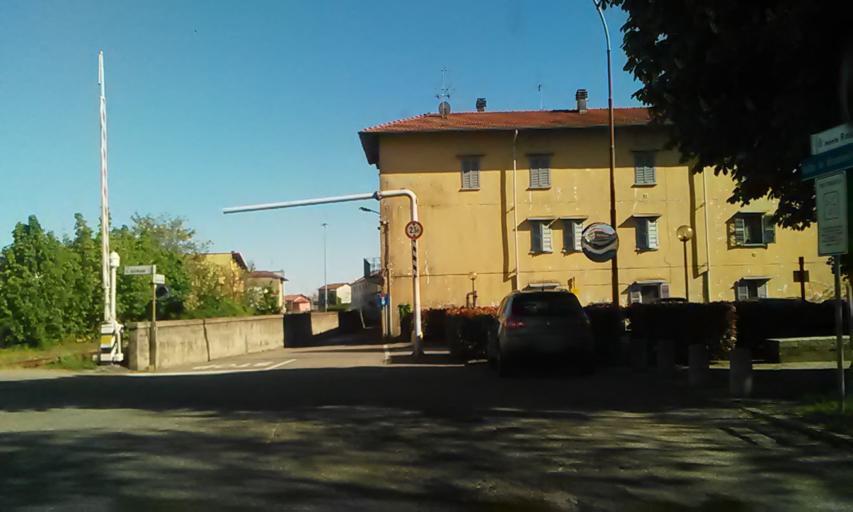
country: IT
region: Piedmont
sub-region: Provincia di Novara
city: Romagnano Sesia
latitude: 45.6323
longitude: 8.3799
